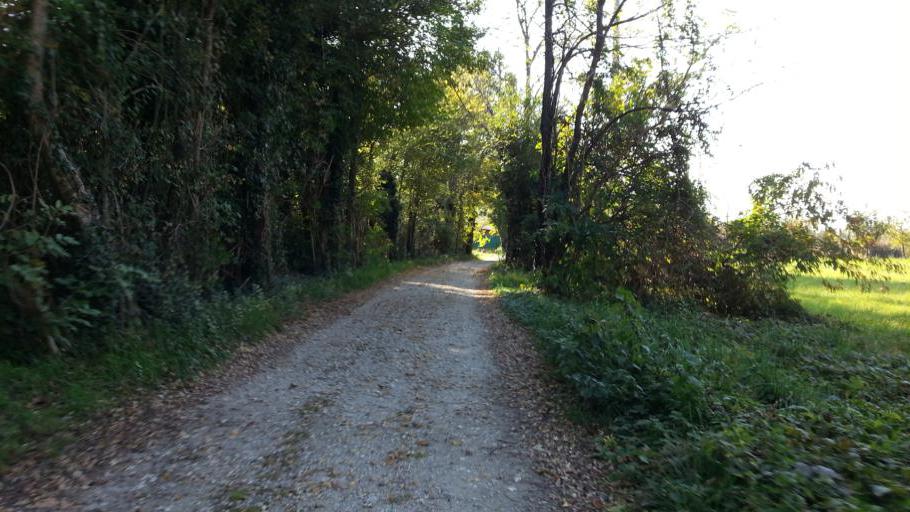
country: IT
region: Friuli Venezia Giulia
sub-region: Provincia di Udine
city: Venzone
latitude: 46.3301
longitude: 13.1325
